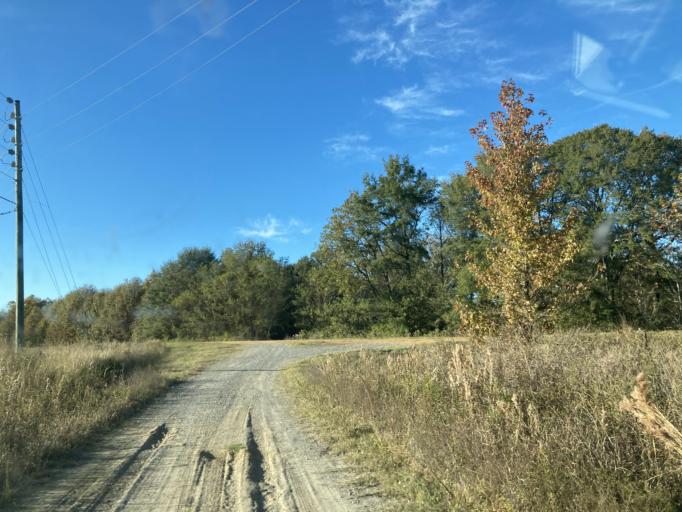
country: US
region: Mississippi
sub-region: Yazoo County
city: Yazoo City
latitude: 32.8959
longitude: -90.4358
